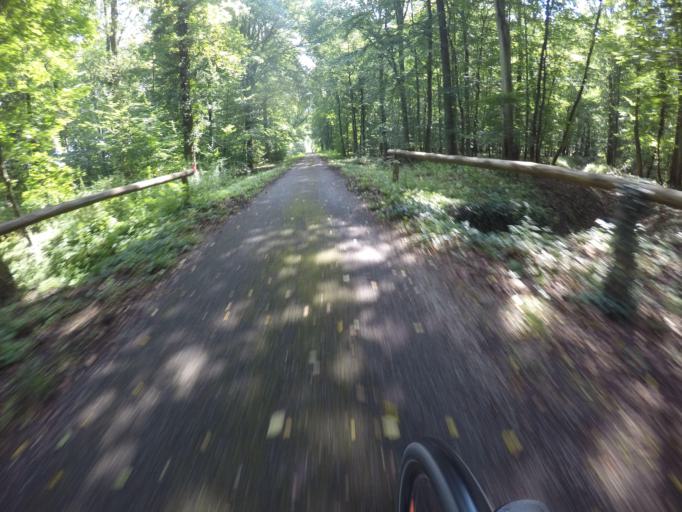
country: DE
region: Baden-Wuerttemberg
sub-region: Karlsruhe Region
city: Hambrucken
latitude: 49.2147
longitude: 8.5827
